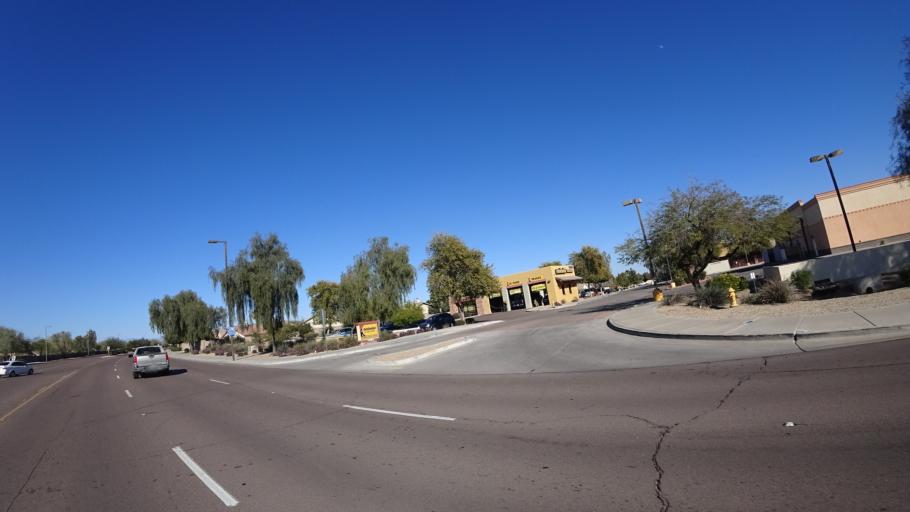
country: US
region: Arizona
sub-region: Maricopa County
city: Sun City West
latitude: 33.6395
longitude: -112.3941
